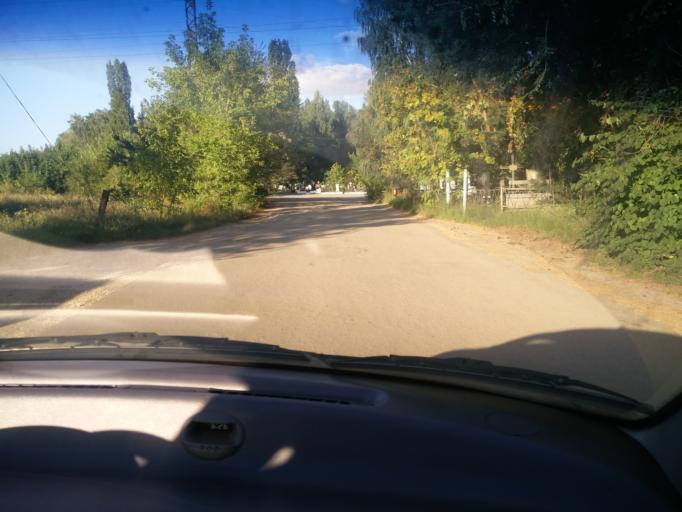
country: RU
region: Voronezj
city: Pridonskoy
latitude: 51.6706
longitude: 39.1054
